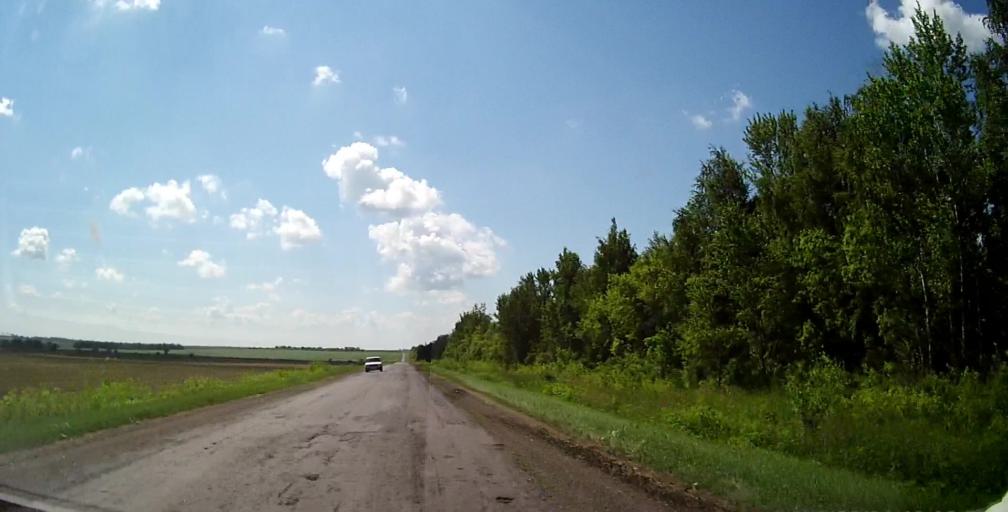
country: RU
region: Lipetsk
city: Chaplygin
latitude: 53.2896
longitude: 39.9583
